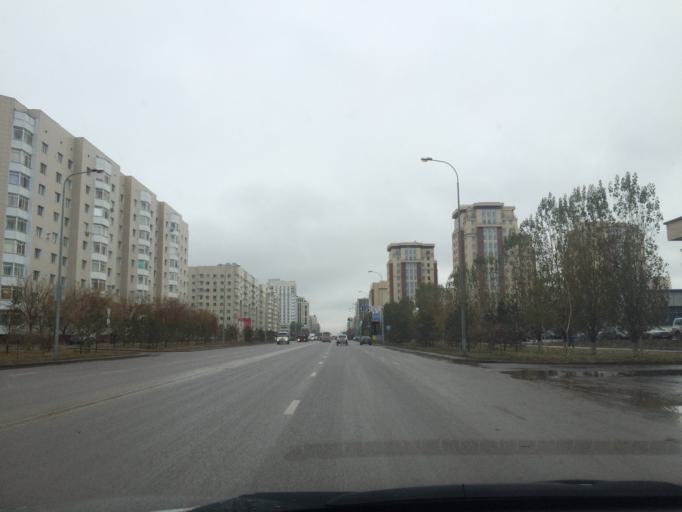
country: KZ
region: Astana Qalasy
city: Astana
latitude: 51.1156
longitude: 71.4147
